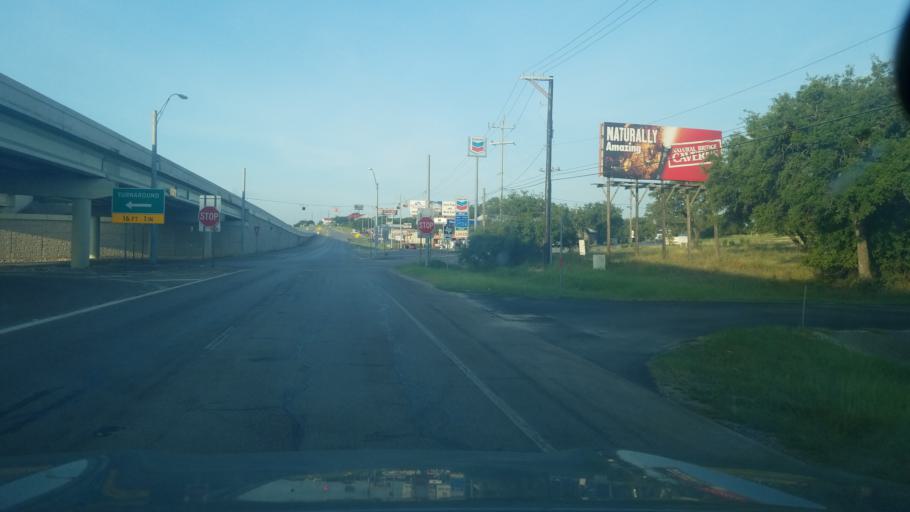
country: US
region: Texas
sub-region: Comal County
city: Bulverde
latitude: 29.7437
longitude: -98.4349
